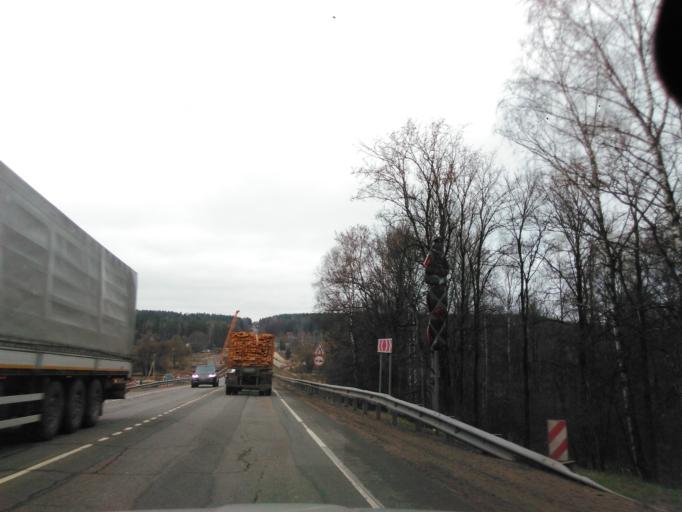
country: RU
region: Moskovskaya
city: Istra
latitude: 55.8604
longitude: 36.9375
